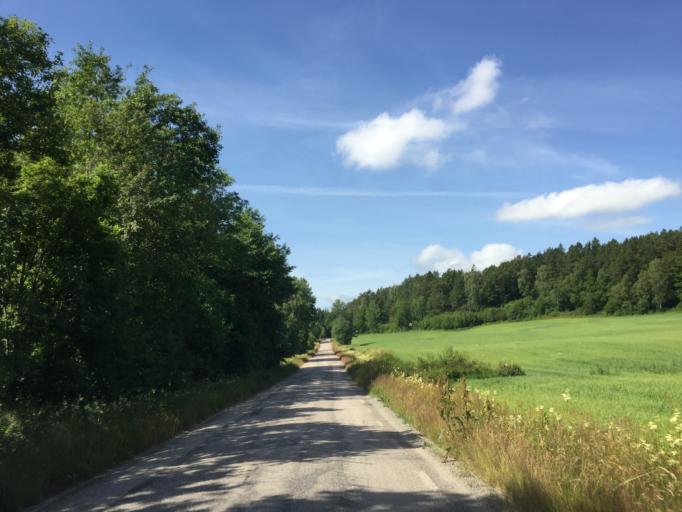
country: SE
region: Vaestra Goetaland
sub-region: Orust
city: Henan
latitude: 58.2915
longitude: 11.6334
